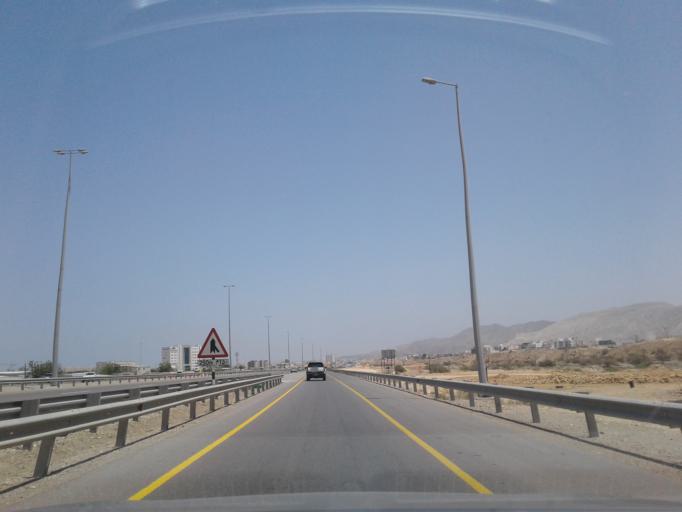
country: OM
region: Muhafazat Masqat
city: Bawshar
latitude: 23.5622
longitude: 58.3455
